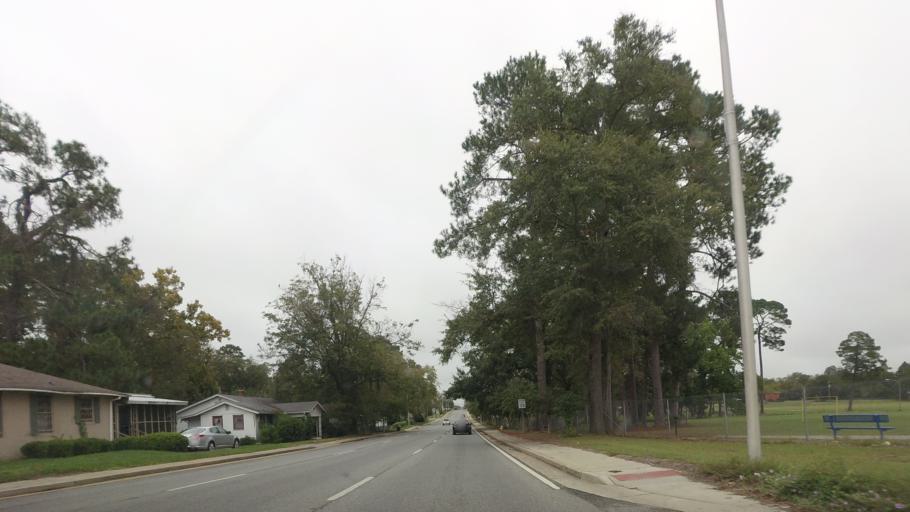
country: US
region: Georgia
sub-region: Ben Hill County
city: Fitzgerald
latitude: 31.7082
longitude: -83.2515
